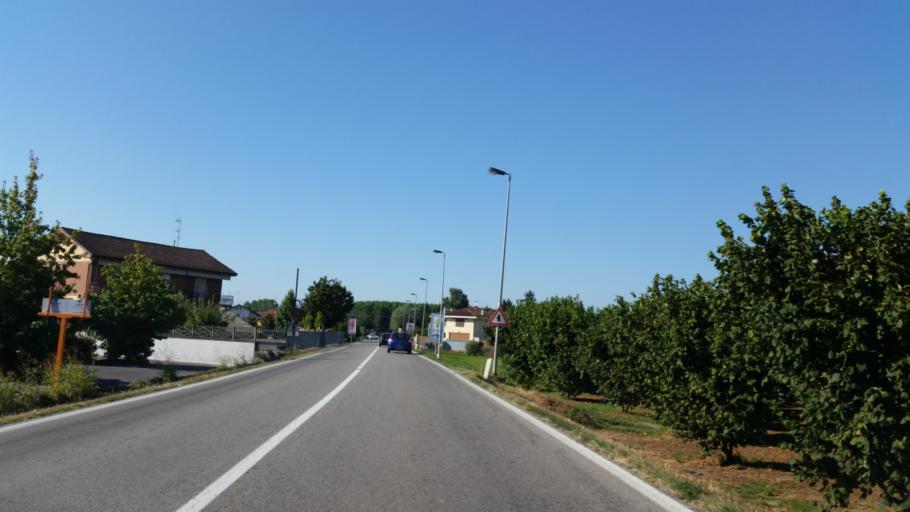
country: IT
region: Piedmont
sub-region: Provincia di Cuneo
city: Cinzano
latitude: 44.6849
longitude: 7.8926
